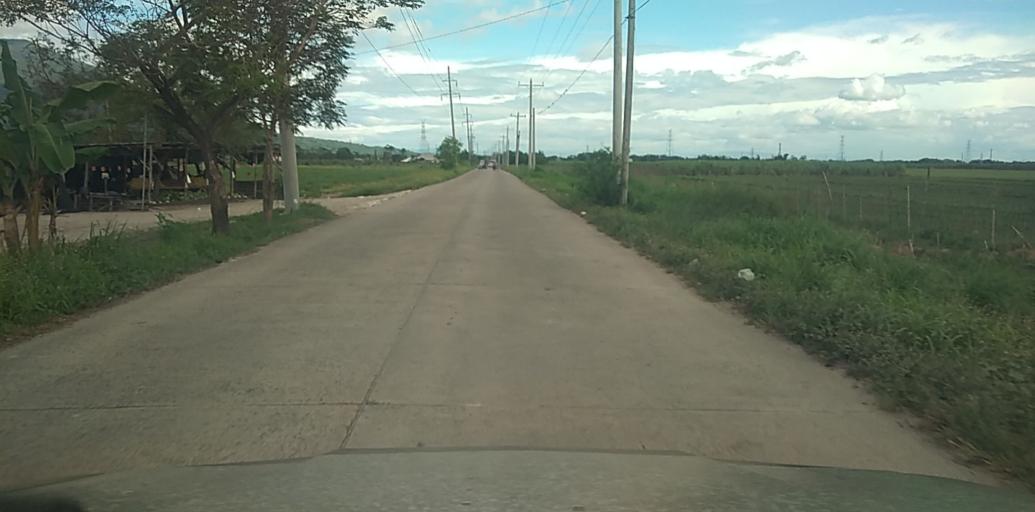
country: PH
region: Central Luzon
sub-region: Province of Pampanga
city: Pandacaqui
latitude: 15.1756
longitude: 120.6694
